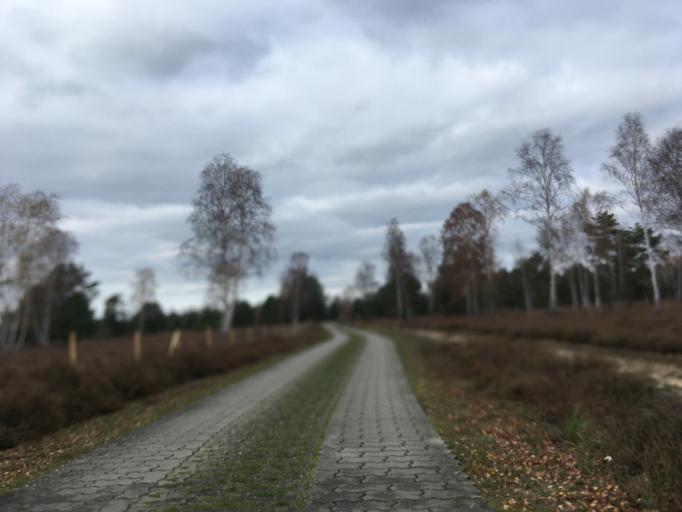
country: DE
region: Brandenburg
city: Tauer
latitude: 52.0051
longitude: 14.5014
